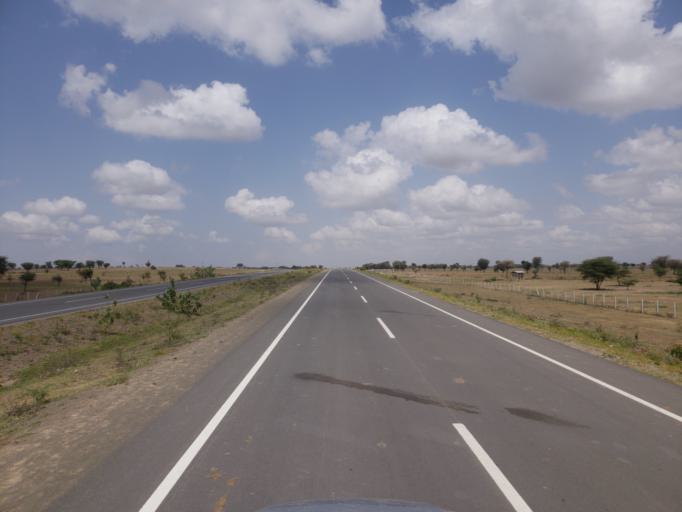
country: ET
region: Oromiya
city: Mojo
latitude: 8.3223
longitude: 38.9559
